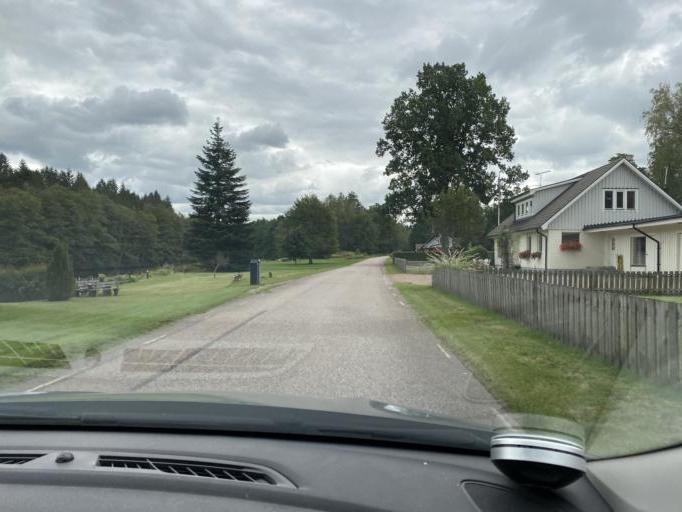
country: SE
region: Kronoberg
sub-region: Markaryds Kommun
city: Markaryd
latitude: 56.4848
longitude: 13.5606
